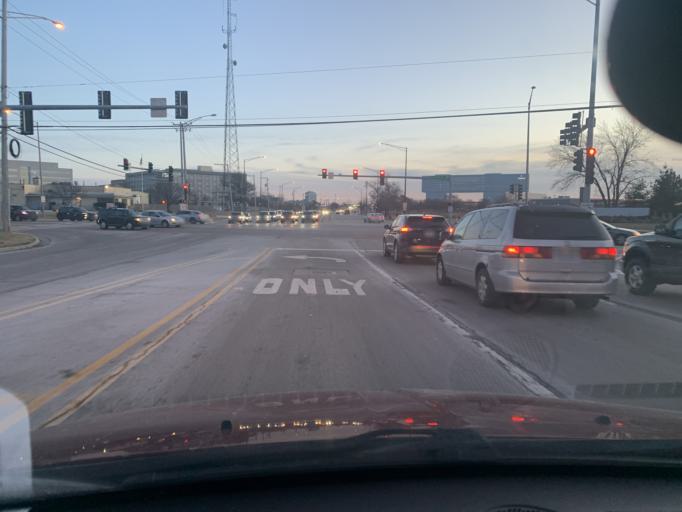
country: US
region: Illinois
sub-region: Cook County
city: Rolling Meadows
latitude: 42.0688
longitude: -88.0439
